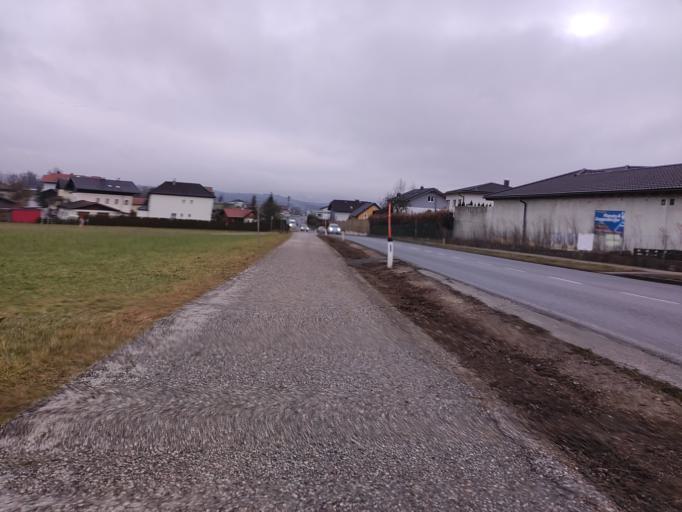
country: AT
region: Salzburg
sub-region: Politischer Bezirk Salzburg-Umgebung
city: Seekirchen am Wallersee
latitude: 47.9057
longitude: 13.1199
